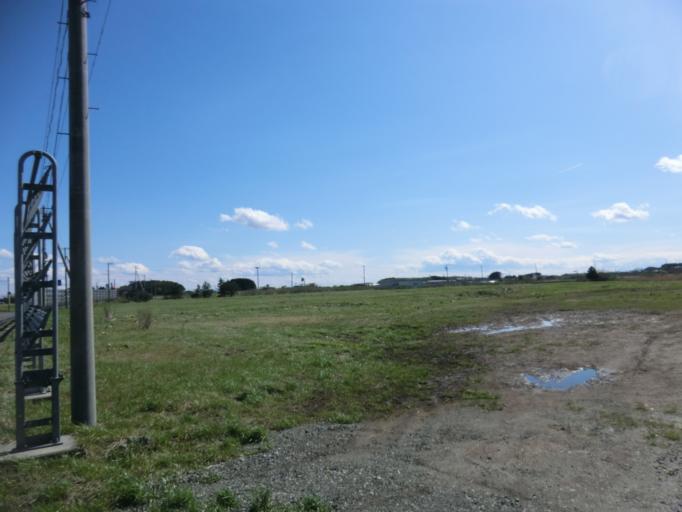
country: JP
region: Aomori
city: Misawa
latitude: 40.6973
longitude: 141.4239
